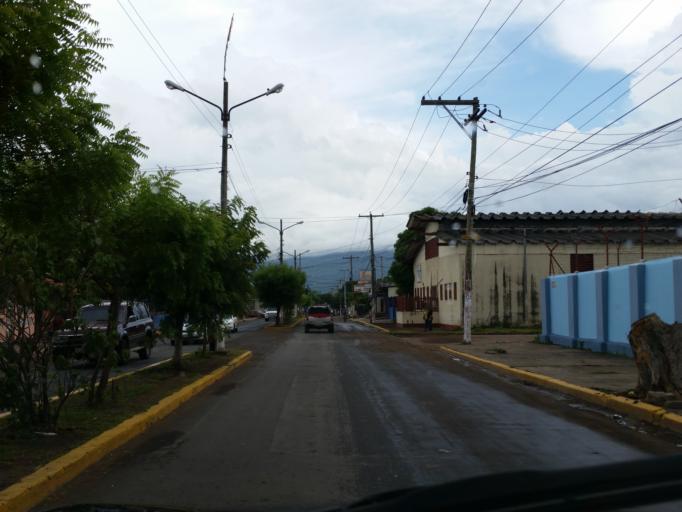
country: NI
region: Granada
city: Granada
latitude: 11.9353
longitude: -85.9625
